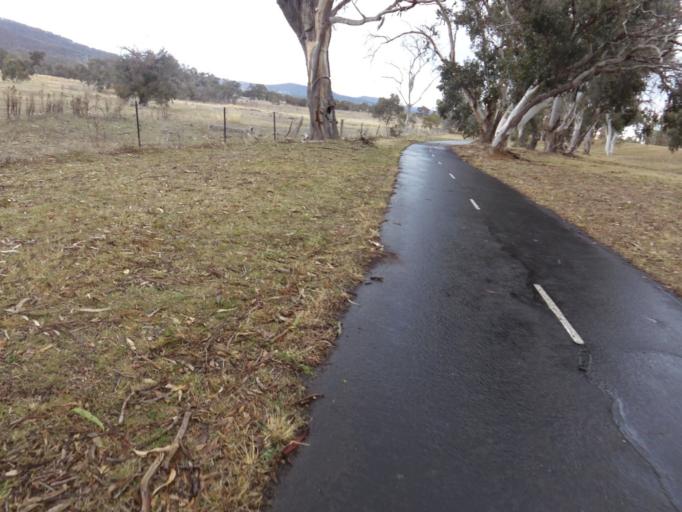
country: AU
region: Australian Capital Territory
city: Macquarie
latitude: -35.2719
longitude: 149.0759
